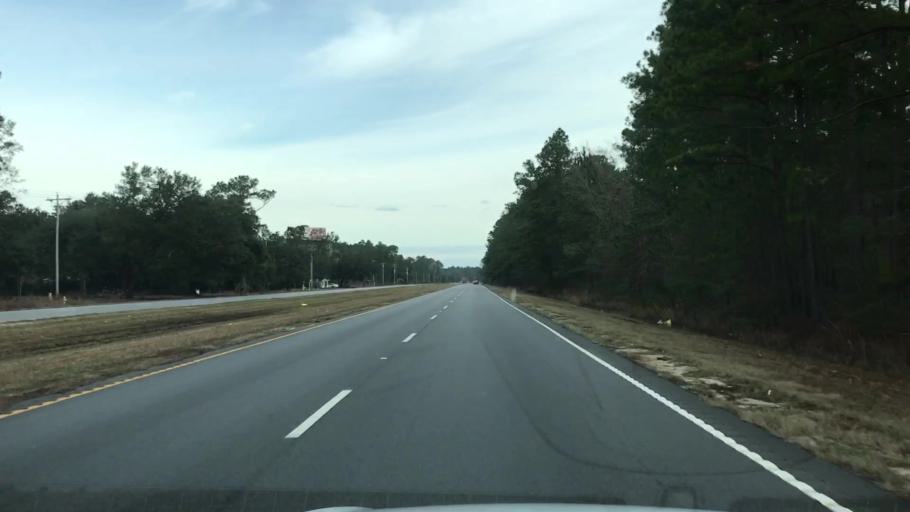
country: US
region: South Carolina
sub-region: Georgetown County
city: Georgetown
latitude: 33.2387
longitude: -79.3756
